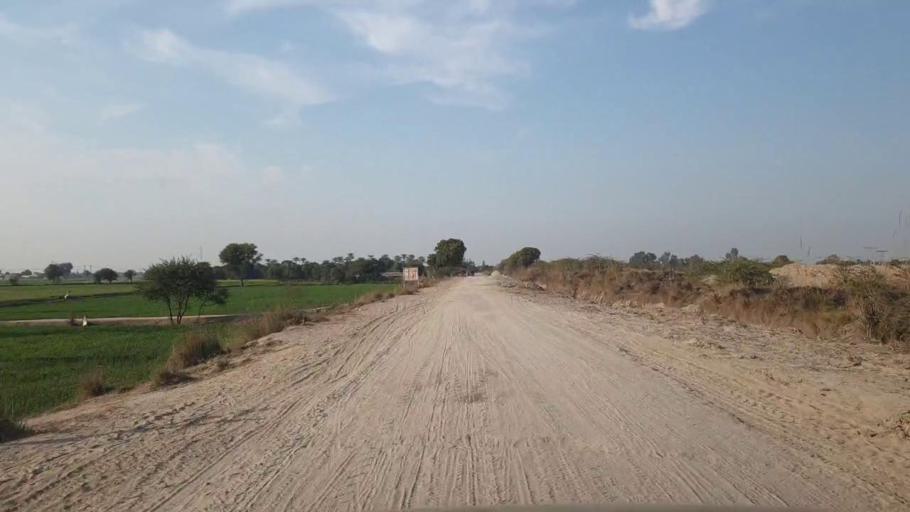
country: PK
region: Sindh
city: Shahpur Chakar
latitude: 26.1509
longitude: 68.6424
